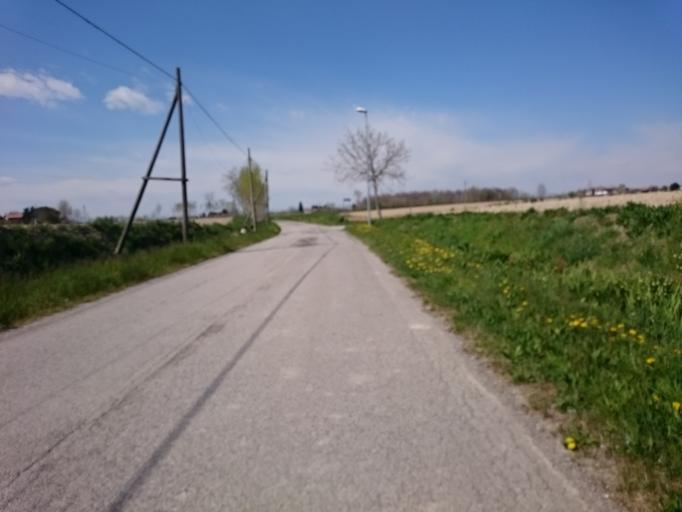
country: IT
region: Veneto
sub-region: Provincia di Padova
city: Brugine
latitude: 45.3060
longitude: 11.9832
